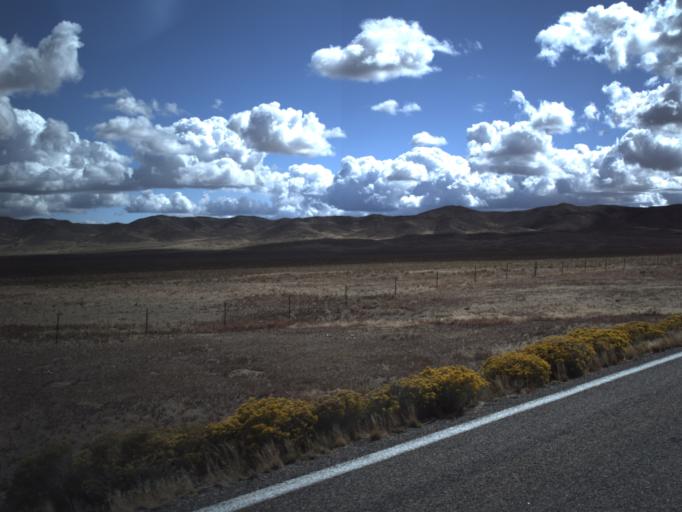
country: US
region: Utah
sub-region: Beaver County
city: Milford
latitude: 38.6648
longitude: -113.8802
